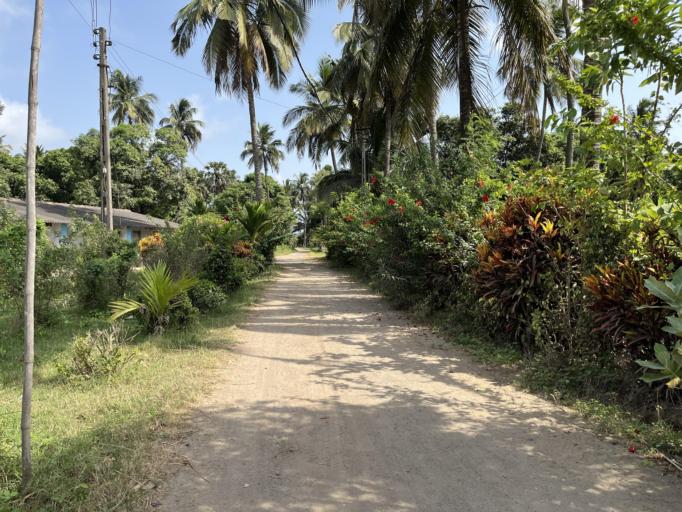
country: IN
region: Daman and Diu
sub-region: Daman District
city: Daman
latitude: 20.3509
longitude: 72.8118
